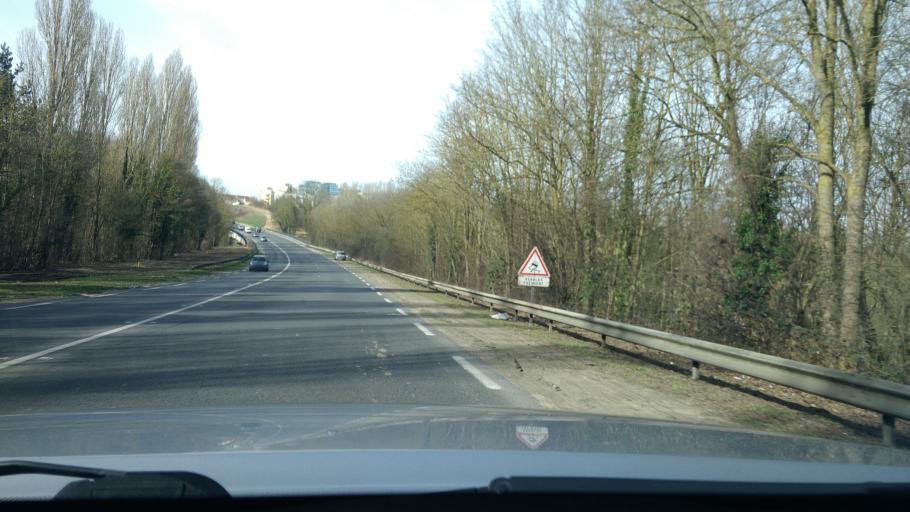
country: FR
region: Ile-de-France
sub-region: Departement de Seine-et-Marne
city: Rubelles
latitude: 48.5471
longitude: 2.6775
